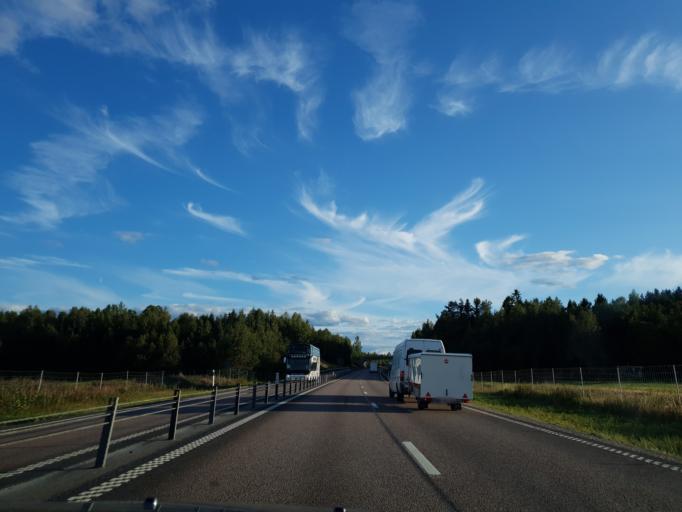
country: SE
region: Gaevleborg
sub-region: Hudiksvalls Kommun
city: Hudiksvall
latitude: 61.7627
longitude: 17.0939
